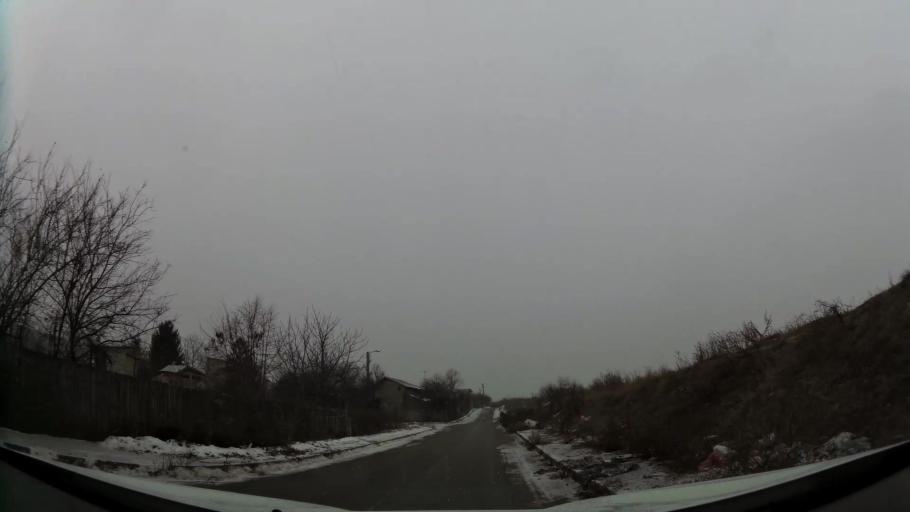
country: RO
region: Prahova
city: Ploiesti
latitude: 44.9549
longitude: 26.0351
